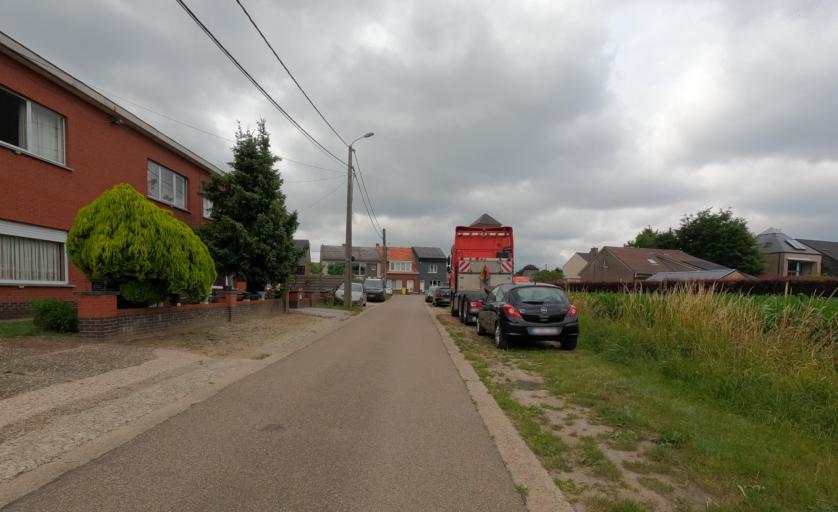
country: BE
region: Flanders
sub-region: Provincie Antwerpen
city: Berlaar
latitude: 51.1377
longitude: 4.6203
